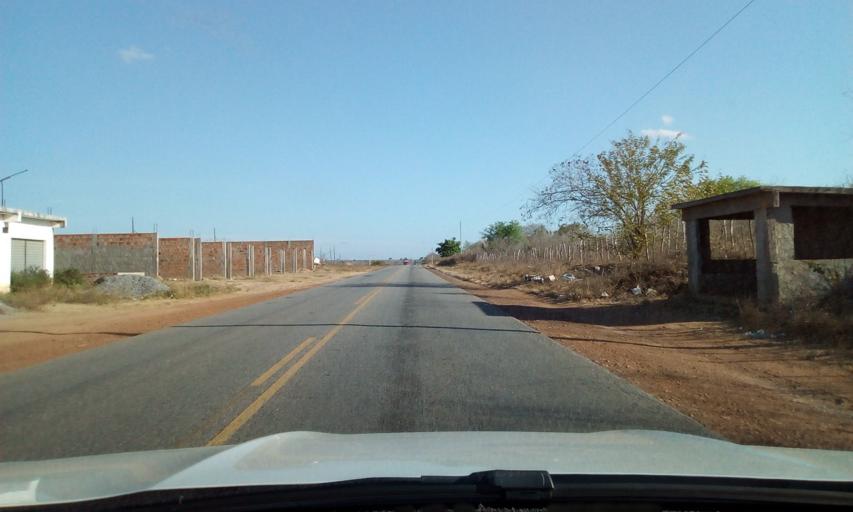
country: BR
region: Paraiba
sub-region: Mulungu
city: Mulungu
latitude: -6.9612
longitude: -35.4113
